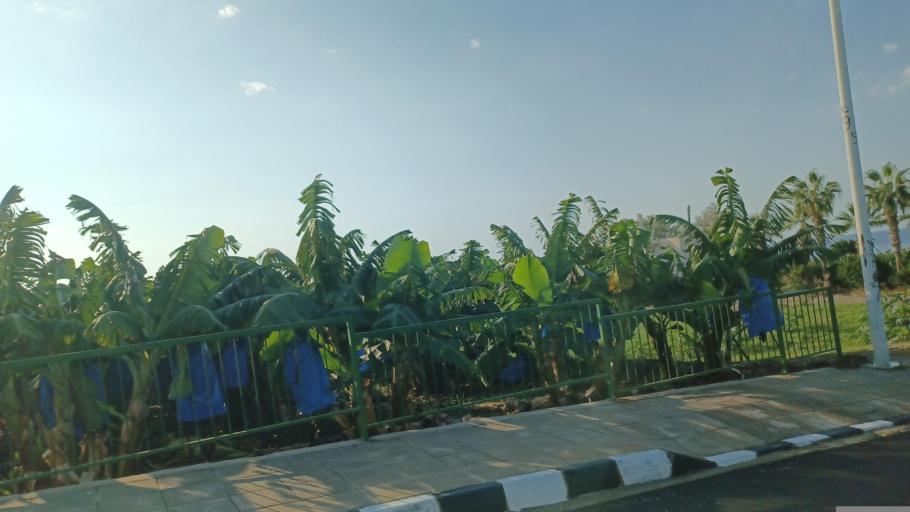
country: CY
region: Pafos
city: Kissonerga
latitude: 34.8222
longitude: 32.3955
